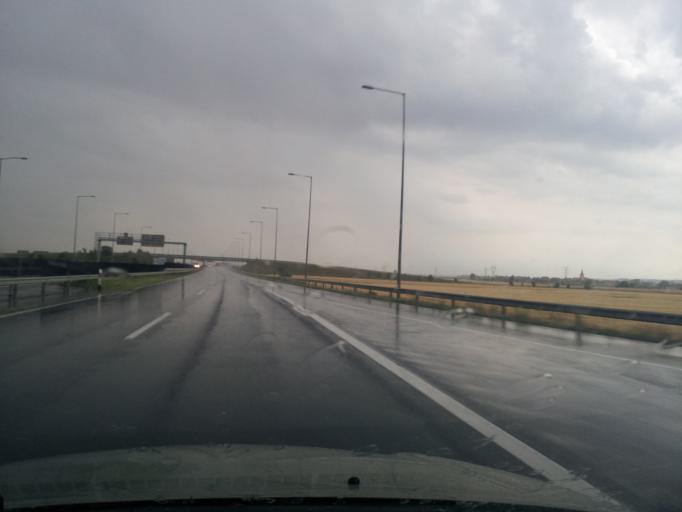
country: HU
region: Borsod-Abauj-Zemplen
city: Alsozsolca
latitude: 48.0591
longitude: 20.8454
